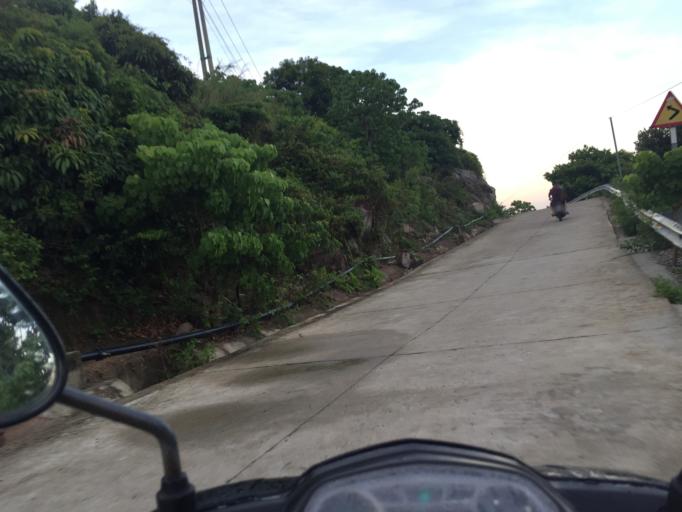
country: VN
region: Quang Nam
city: Hoi An
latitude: 15.9533
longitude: 108.5086
